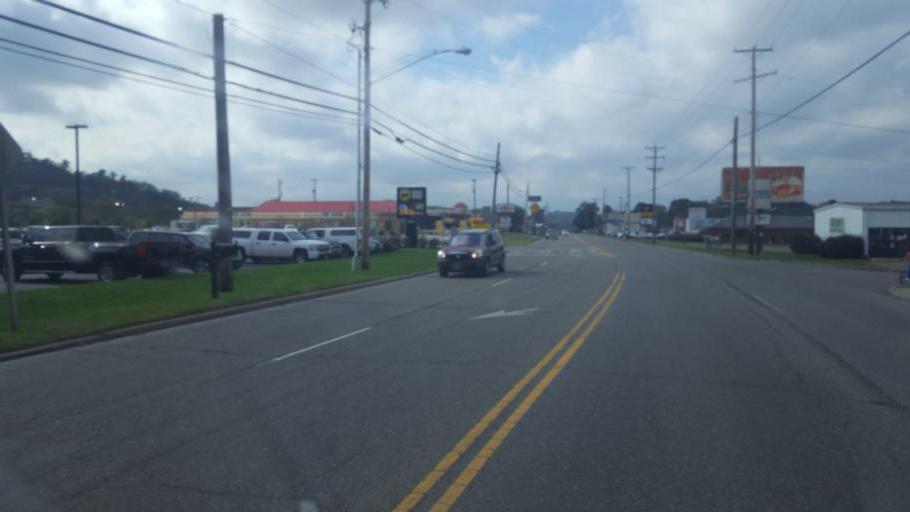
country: US
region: Ohio
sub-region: Tuscarawas County
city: New Philadelphia
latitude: 40.4931
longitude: -81.4662
